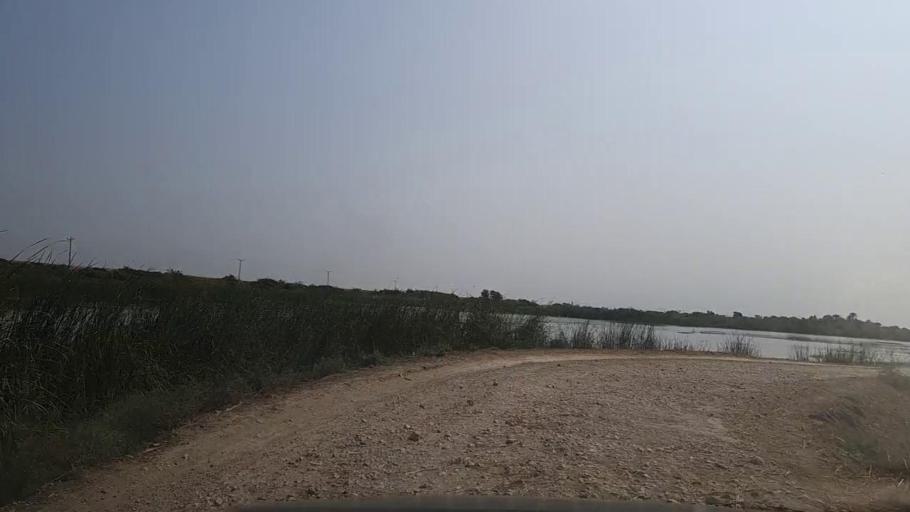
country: PK
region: Sindh
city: Chuhar Jamali
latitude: 24.5487
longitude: 67.9182
